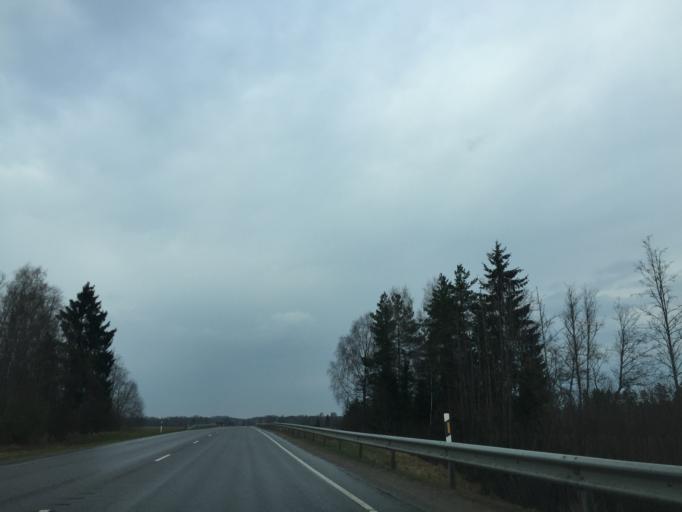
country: EE
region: Tartu
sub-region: UElenurme vald
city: Ulenurme
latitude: 58.0819
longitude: 26.7349
